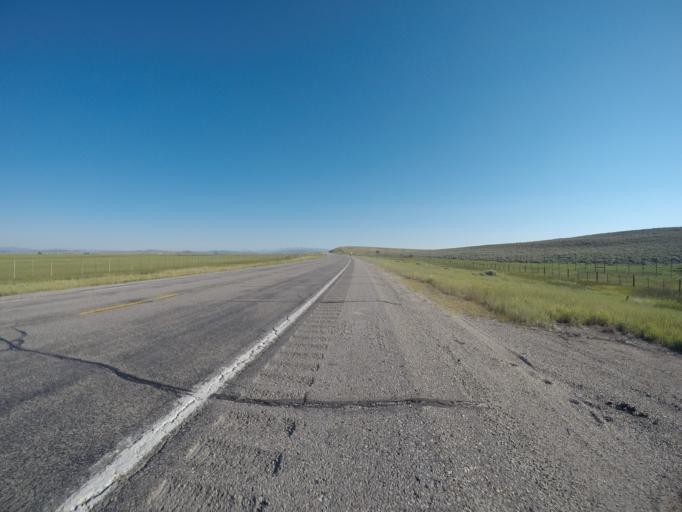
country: US
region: Wyoming
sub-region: Sublette County
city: Pinedale
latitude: 42.9353
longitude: -110.0814
